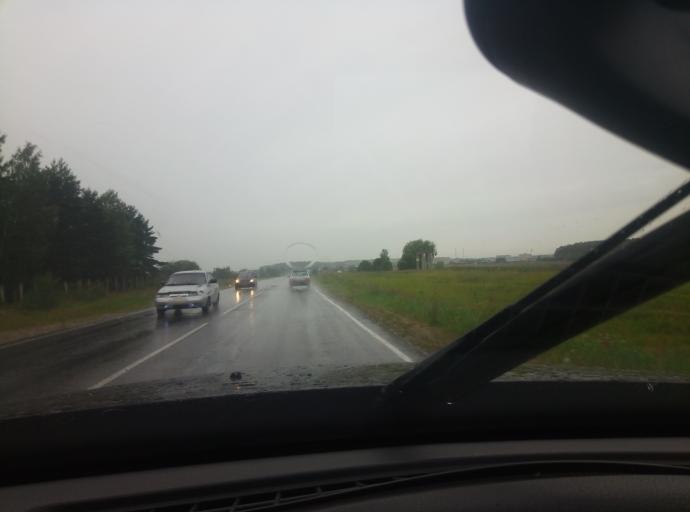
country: RU
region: Kaluga
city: Kremenki
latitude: 54.8776
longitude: 37.1427
